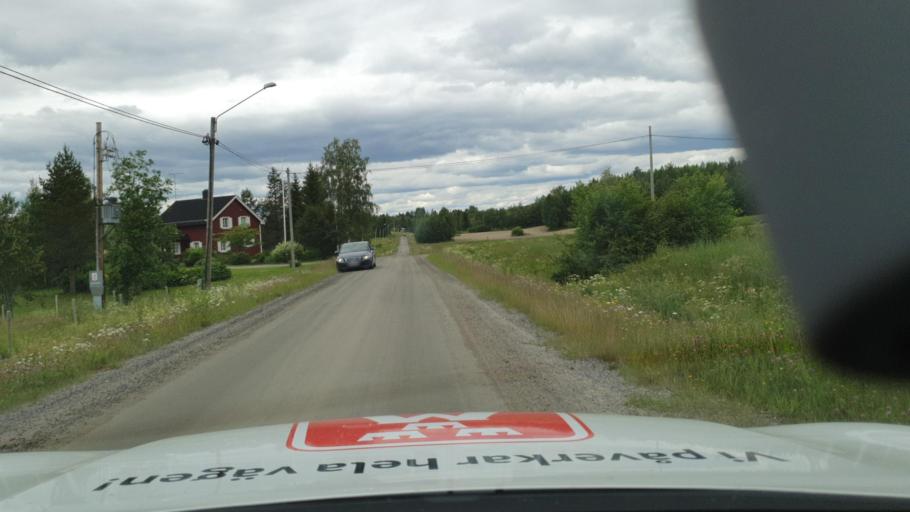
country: SE
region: Vaesterbotten
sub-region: Bjurholms Kommun
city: Bjurholm
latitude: 63.7215
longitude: 19.3189
